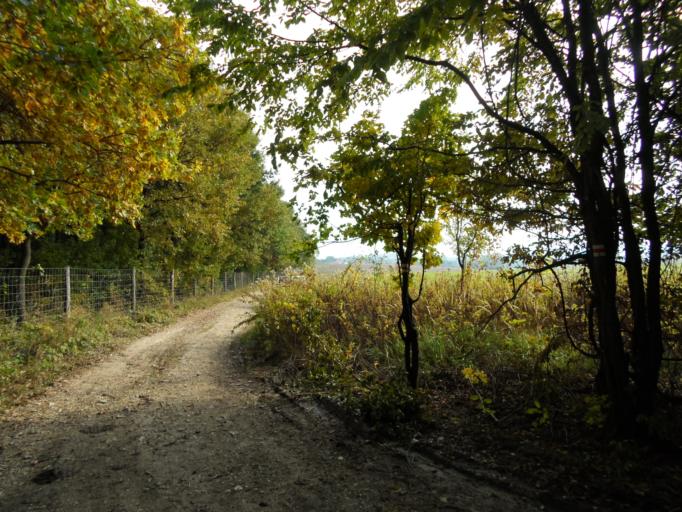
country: HU
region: Veszprem
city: Zirc
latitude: 47.3135
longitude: 17.9127
